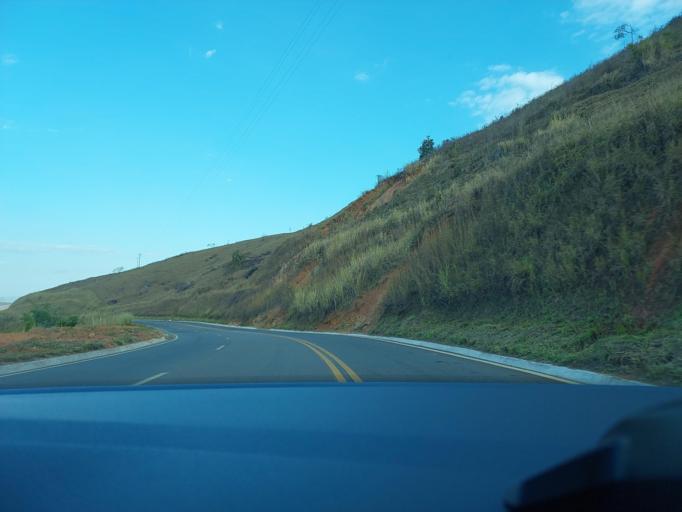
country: BR
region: Minas Gerais
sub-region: Muriae
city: Muriae
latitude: -21.0964
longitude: -42.4710
